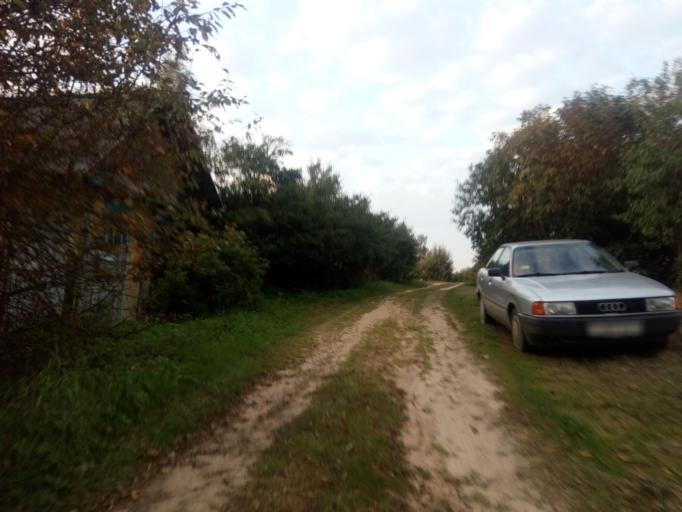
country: BY
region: Vitebsk
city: Dzisna
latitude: 55.6559
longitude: 28.3288
